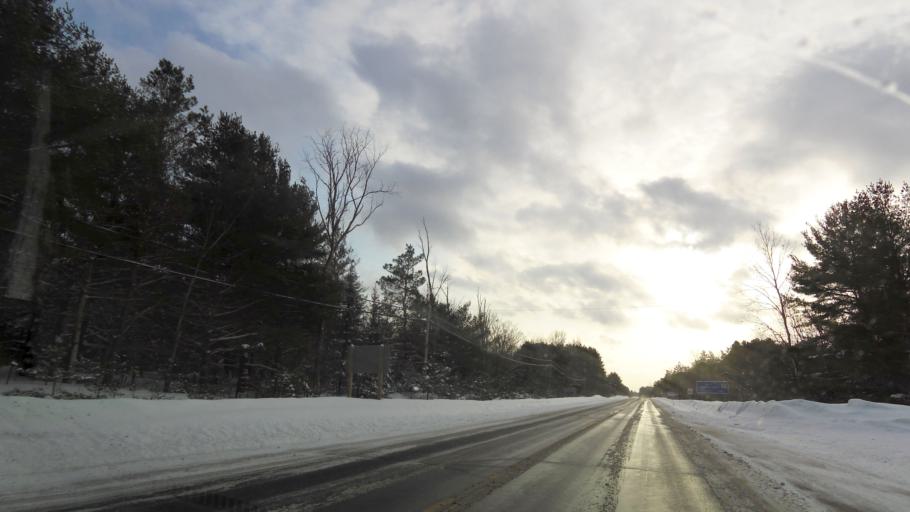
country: CA
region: Ontario
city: Omemee
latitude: 44.7723
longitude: -78.8139
